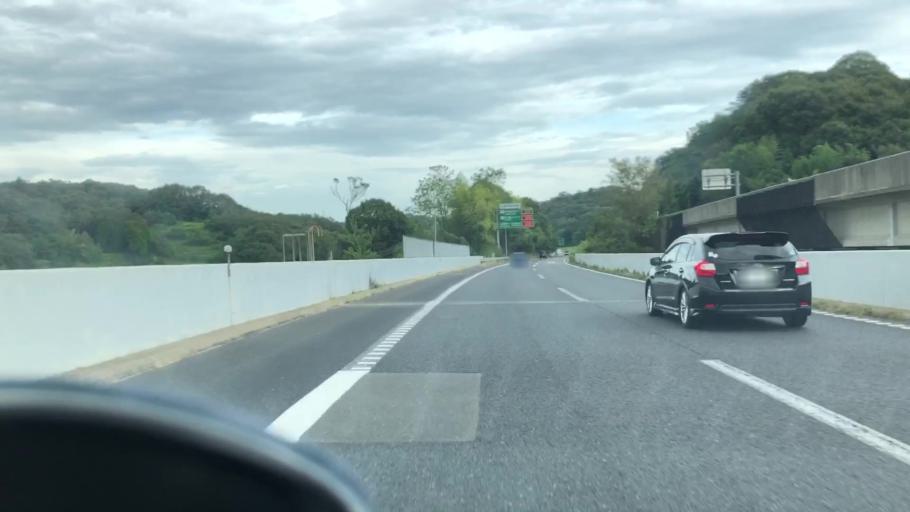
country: JP
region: Hyogo
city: Sandacho
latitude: 34.8912
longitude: 135.1257
